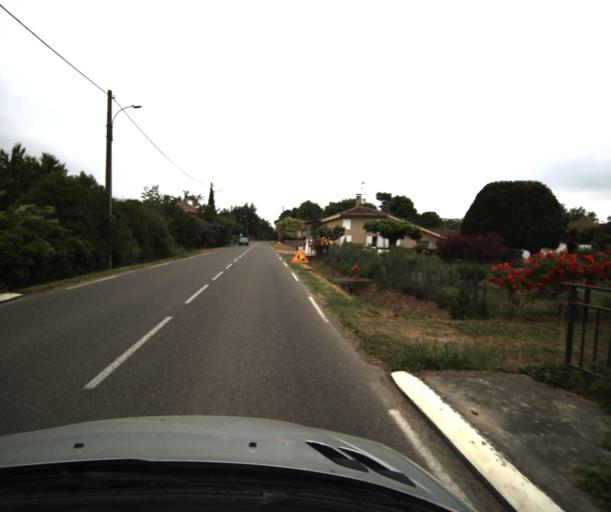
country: FR
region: Midi-Pyrenees
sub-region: Departement du Tarn-et-Garonne
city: Saint-Nicolas-de-la-Grave
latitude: 44.0600
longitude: 1.0247
